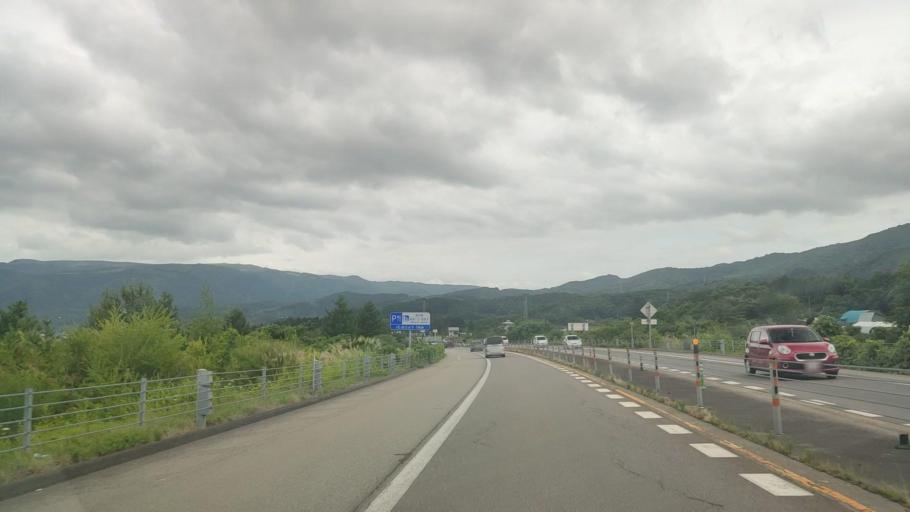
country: JP
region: Hokkaido
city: Nanae
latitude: 41.9189
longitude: 140.6815
